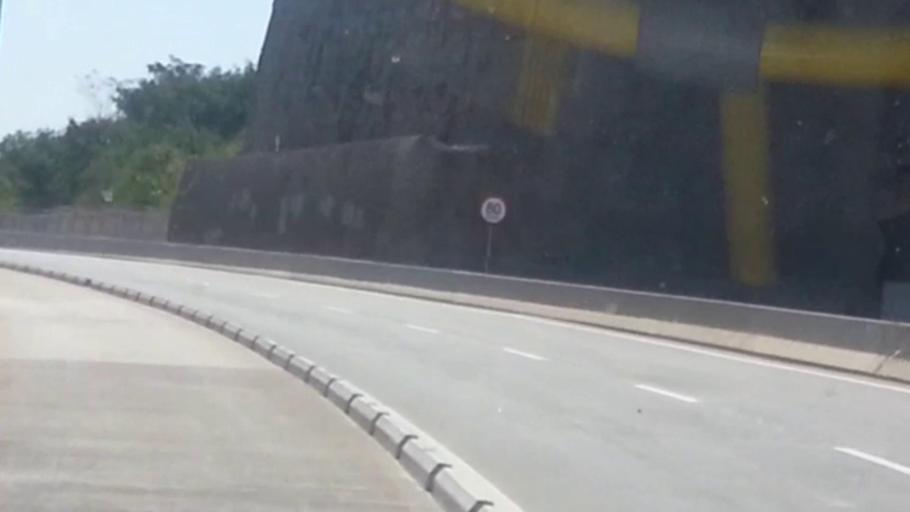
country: BR
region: Rio de Janeiro
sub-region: Nilopolis
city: Nilopolis
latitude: -22.8845
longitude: -43.4002
